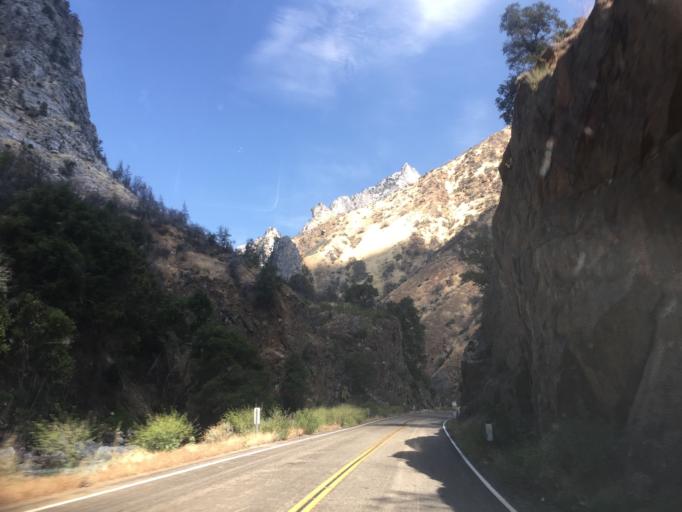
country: US
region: California
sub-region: Tulare County
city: Three Rivers
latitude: 36.8123
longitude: -118.8151
